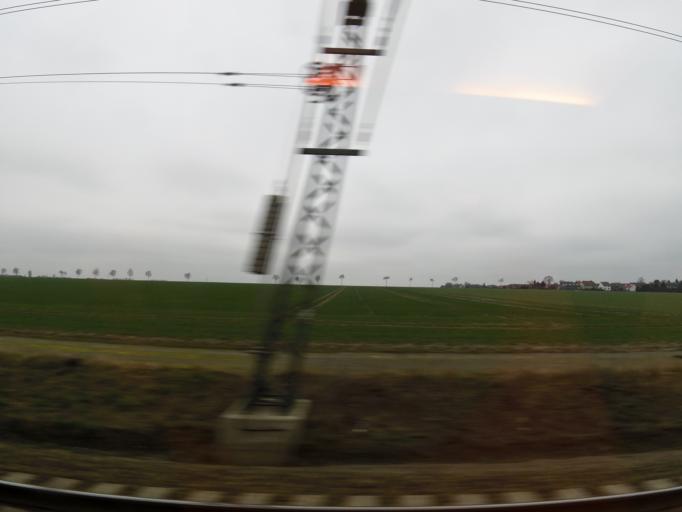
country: DE
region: Lower Saxony
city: Leiferde
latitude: 52.2321
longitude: 10.4464
